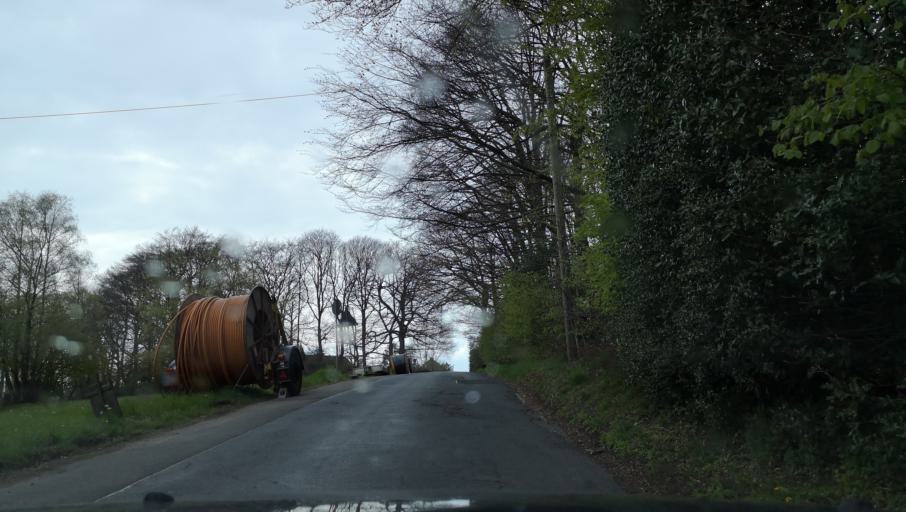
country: DE
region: North Rhine-Westphalia
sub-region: Regierungsbezirk Dusseldorf
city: Remscheid
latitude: 51.2135
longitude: 7.1950
